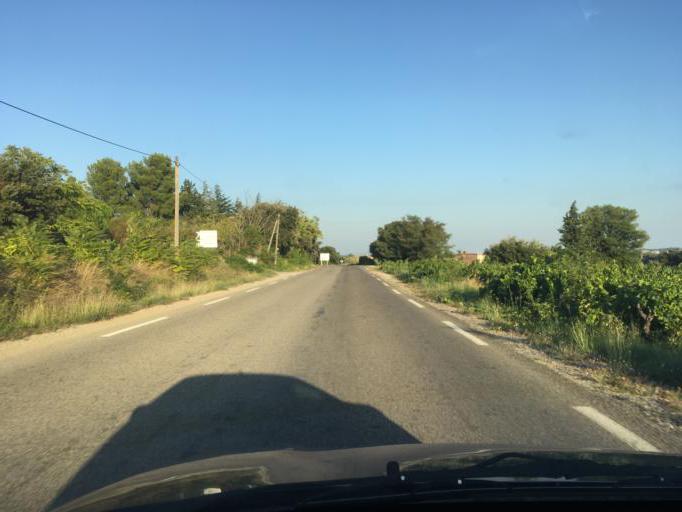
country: FR
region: Languedoc-Roussillon
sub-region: Departement du Gard
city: Tavel
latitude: 44.0096
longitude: 4.7177
